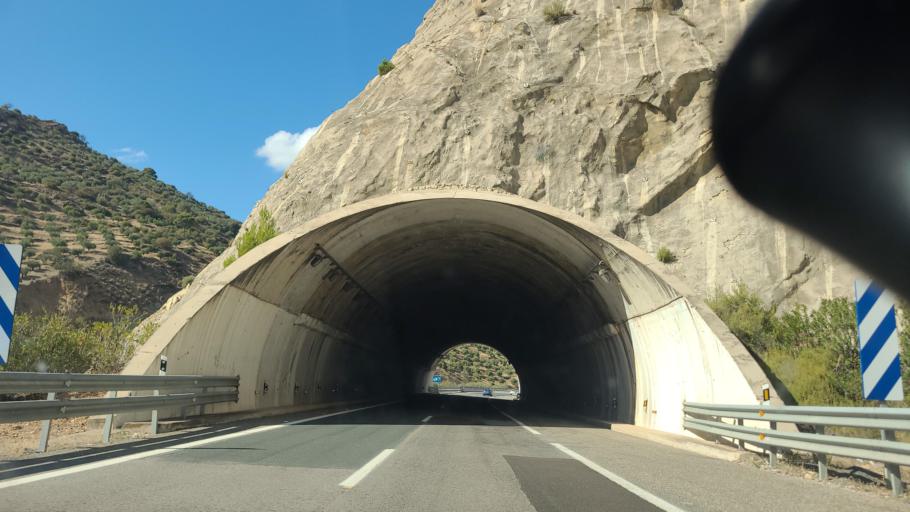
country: ES
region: Andalusia
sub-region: Provincia de Jaen
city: Cambil
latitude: 37.6628
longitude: -3.6153
